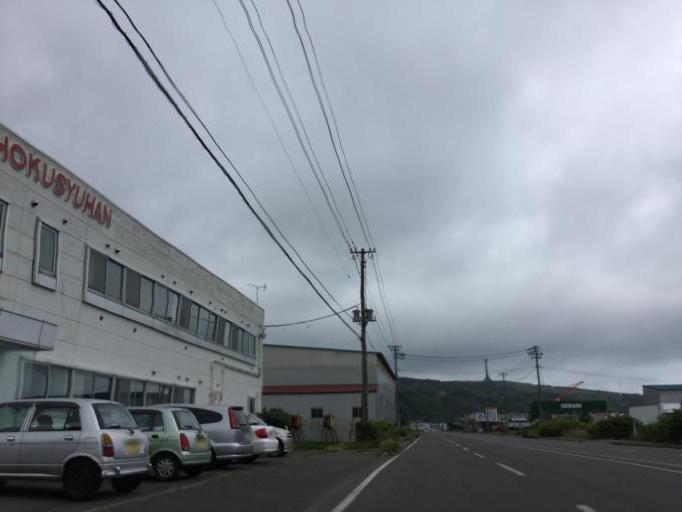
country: JP
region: Hokkaido
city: Wakkanai
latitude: 45.4025
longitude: 141.6853
